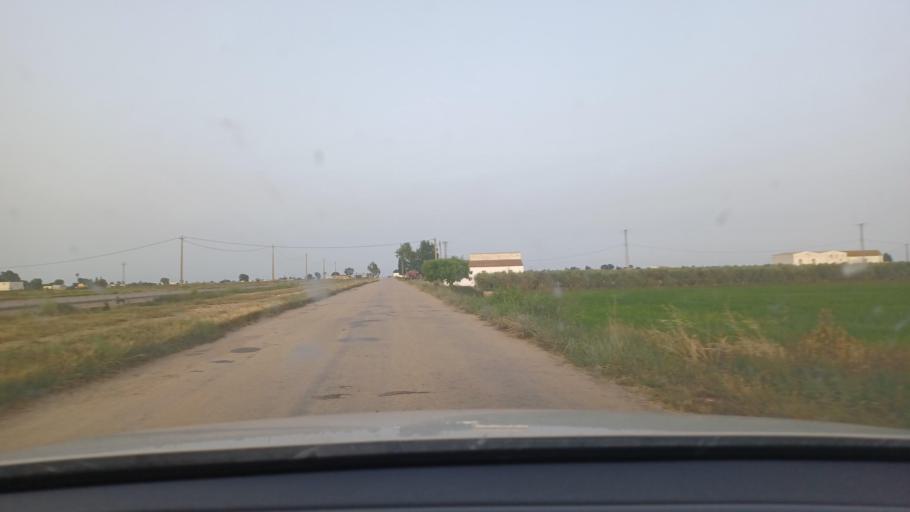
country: ES
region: Catalonia
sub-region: Provincia de Tarragona
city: Amposta
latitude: 40.7006
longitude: 0.6040
